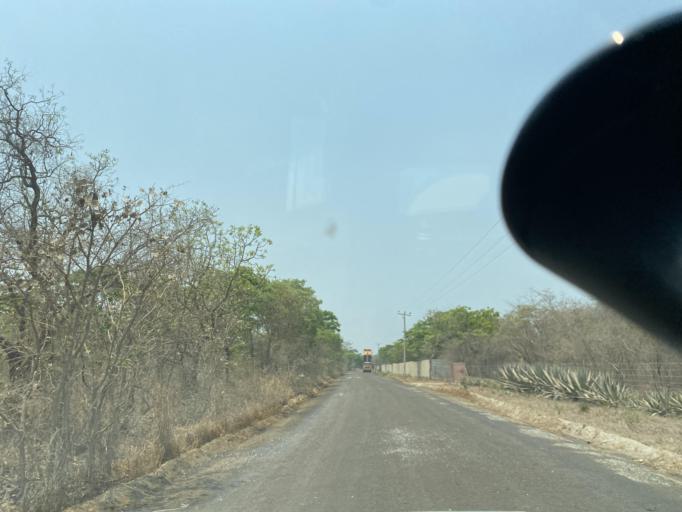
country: ZM
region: Lusaka
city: Lusaka
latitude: -15.5098
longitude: 28.4451
